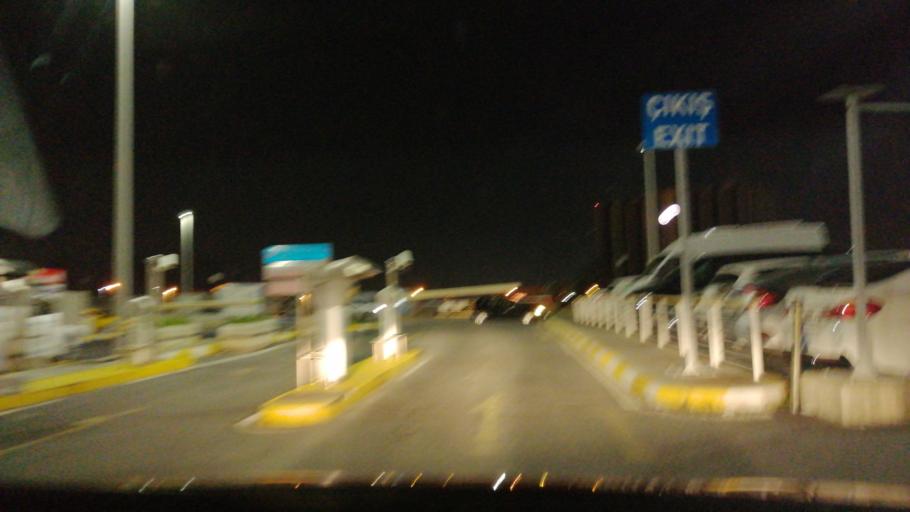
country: TR
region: Istanbul
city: Bahcelievler
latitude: 40.9801
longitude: 28.8248
